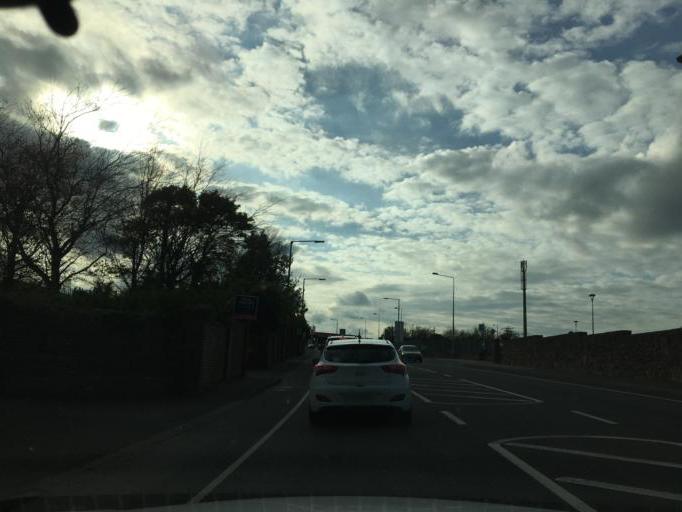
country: IE
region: Leinster
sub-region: Loch Garman
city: Loch Garman
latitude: 52.3419
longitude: -6.4831
